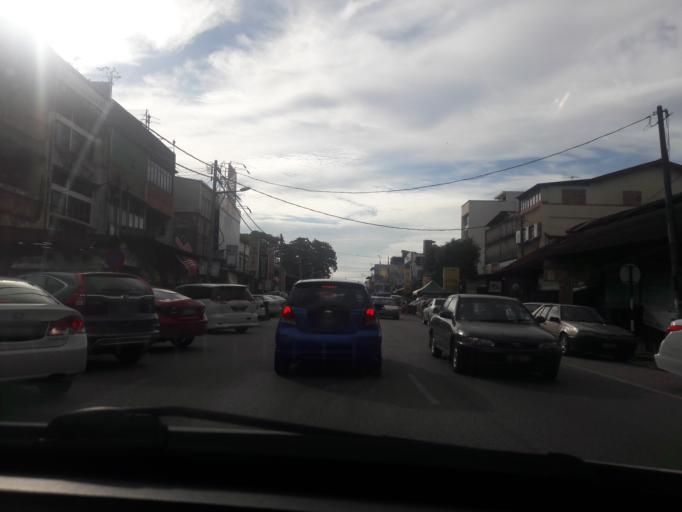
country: MY
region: Kedah
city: Sungai Petani
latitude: 5.6376
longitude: 100.4951
